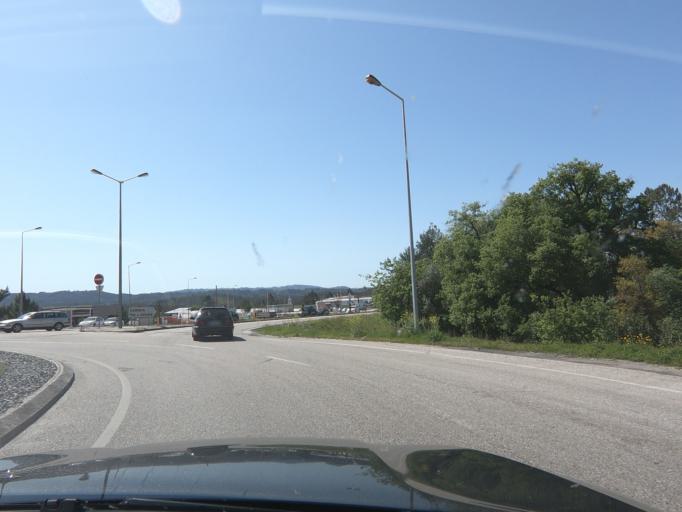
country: PT
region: Coimbra
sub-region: Lousa
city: Lousa
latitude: 40.1292
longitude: -8.2482
